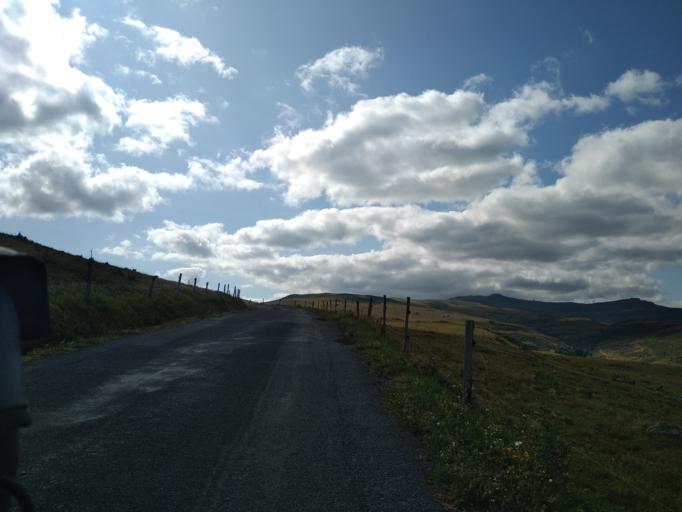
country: FR
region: Auvergne
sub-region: Departement du Cantal
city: Murat
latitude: 45.0266
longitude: 2.8237
